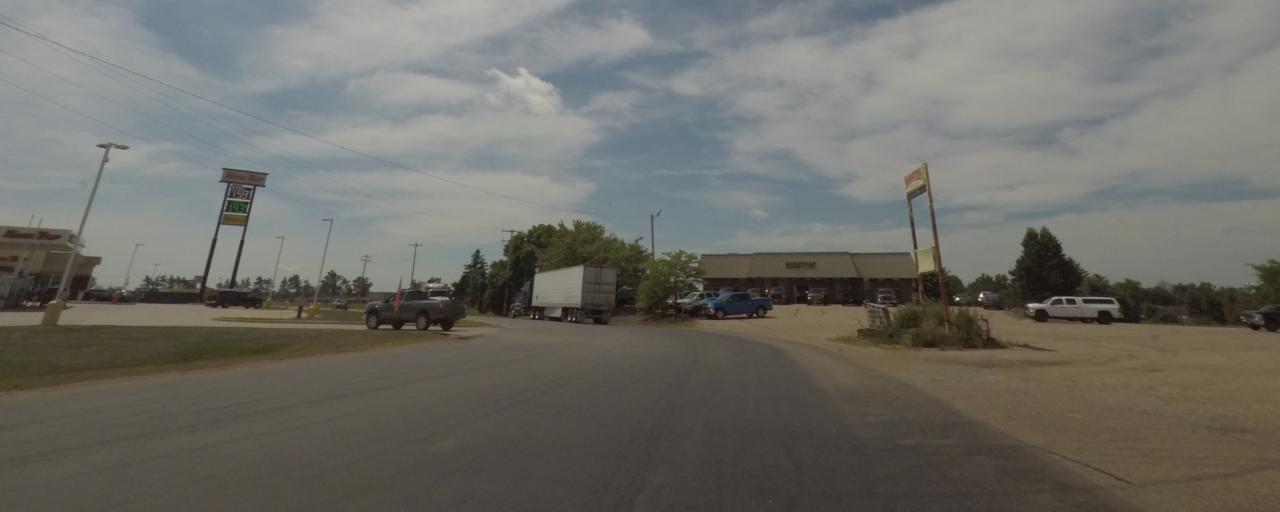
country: US
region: Wisconsin
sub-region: Portage County
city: Plover
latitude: 44.4283
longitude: -89.5157
